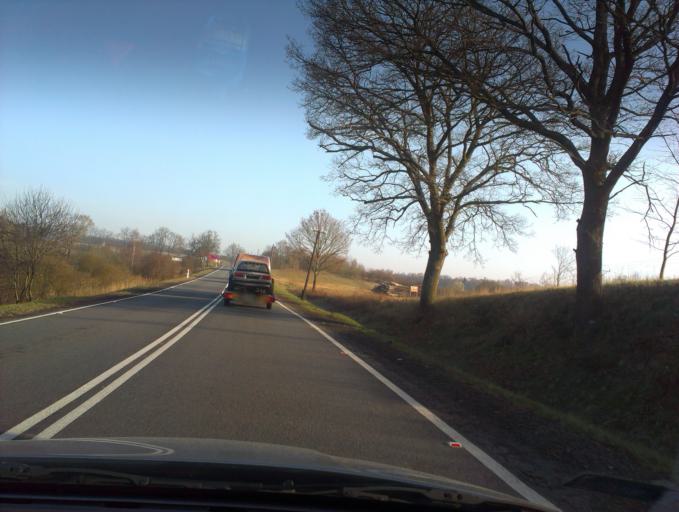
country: PL
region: West Pomeranian Voivodeship
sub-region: Powiat koszalinski
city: Bobolice
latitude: 53.8694
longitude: 16.6149
